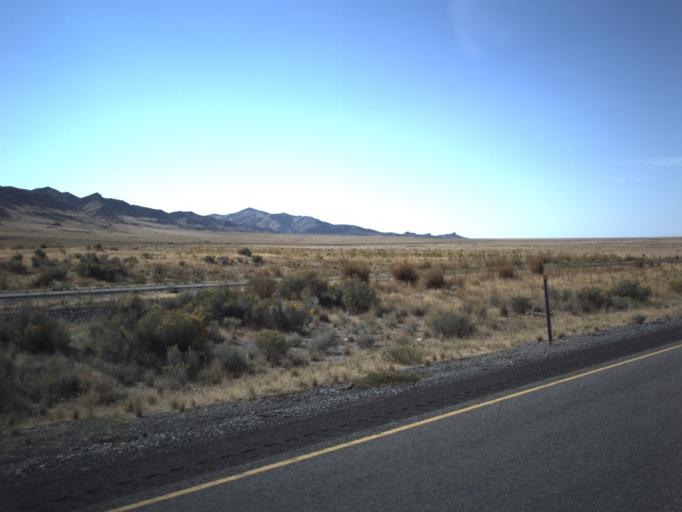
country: US
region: Utah
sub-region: Tooele County
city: Grantsville
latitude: 40.8024
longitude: -112.9406
